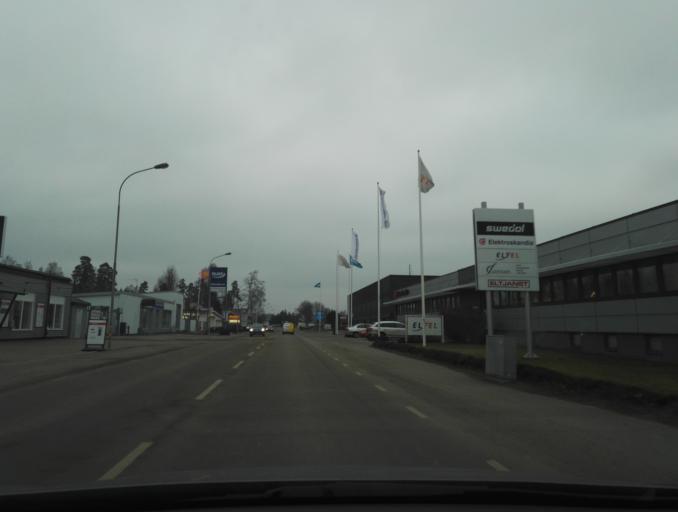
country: SE
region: Kronoberg
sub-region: Vaxjo Kommun
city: Vaexjoe
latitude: 56.8850
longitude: 14.7798
